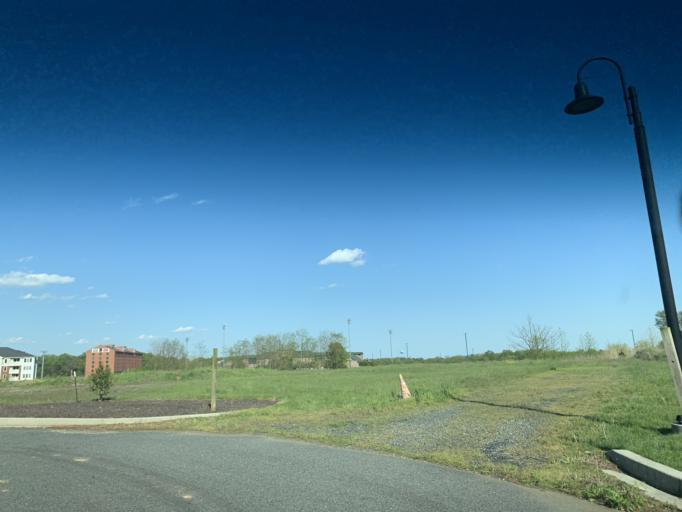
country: US
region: Maryland
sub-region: Harford County
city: Aberdeen
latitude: 39.5313
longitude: -76.1911
